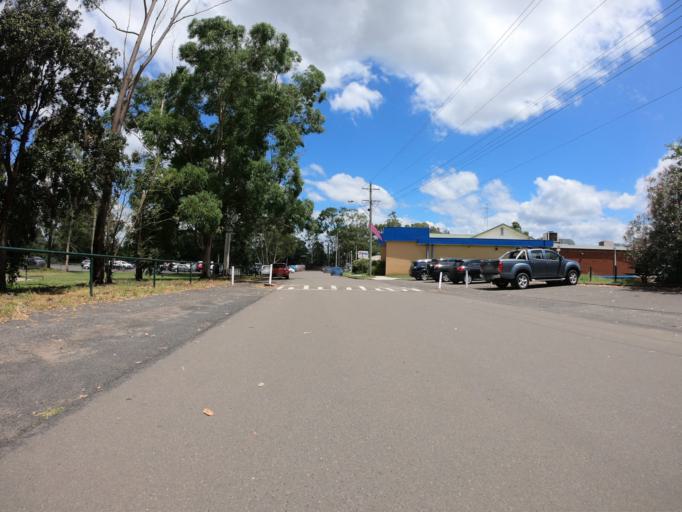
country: AU
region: New South Wales
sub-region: Penrith Municipality
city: Penrith
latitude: -33.7457
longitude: 150.6842
